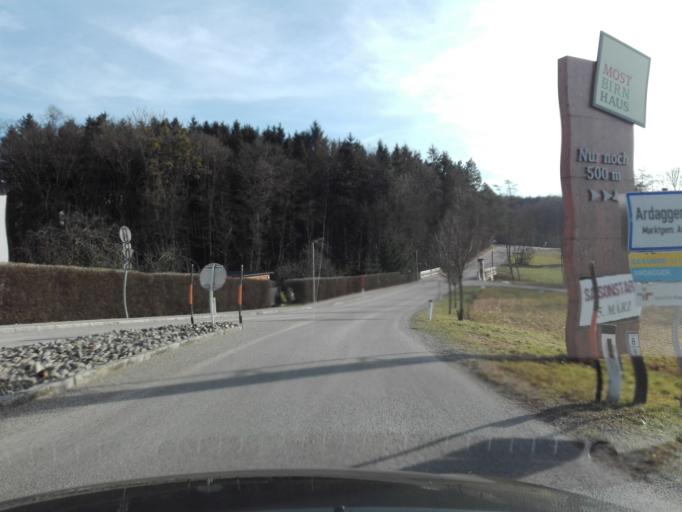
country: AT
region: Lower Austria
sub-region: Politischer Bezirk Amstetten
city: Amstetten
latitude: 48.1640
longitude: 14.8433
